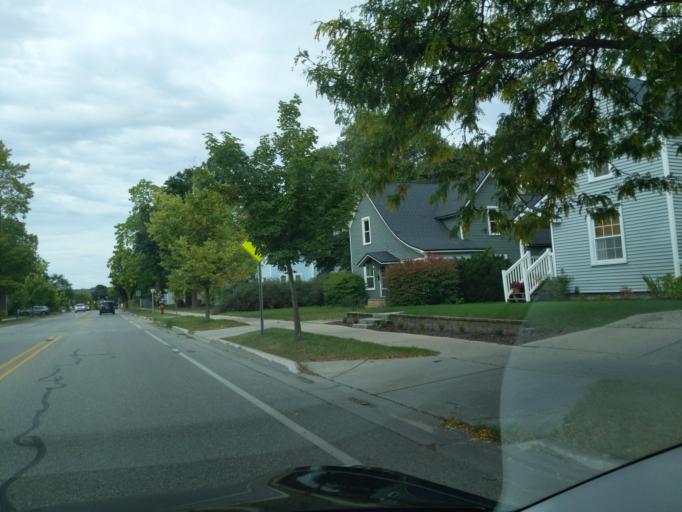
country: US
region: Michigan
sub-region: Grand Traverse County
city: Traverse City
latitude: 44.7590
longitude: -85.6033
